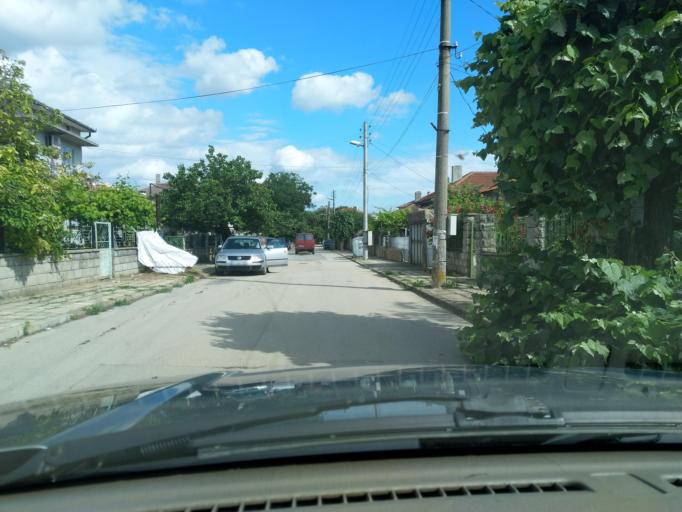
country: BG
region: Dobrich
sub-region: Obshtina Kavarna
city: Kavarna
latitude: 43.4328
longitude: 28.3321
